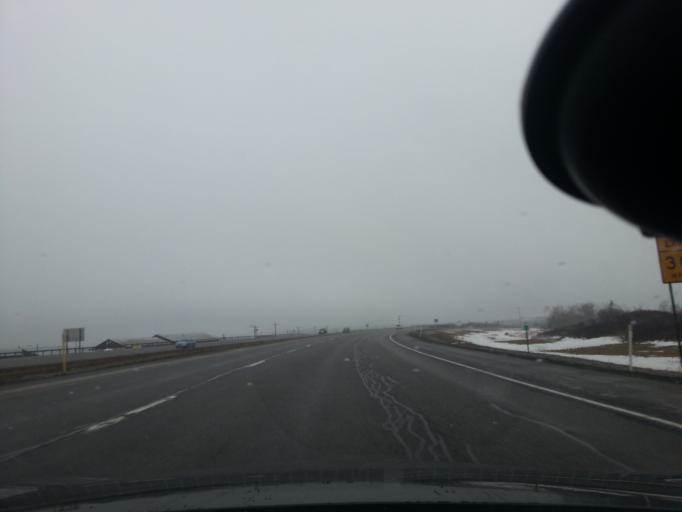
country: US
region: New York
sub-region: Jefferson County
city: Watertown
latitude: 44.0030
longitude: -75.9153
